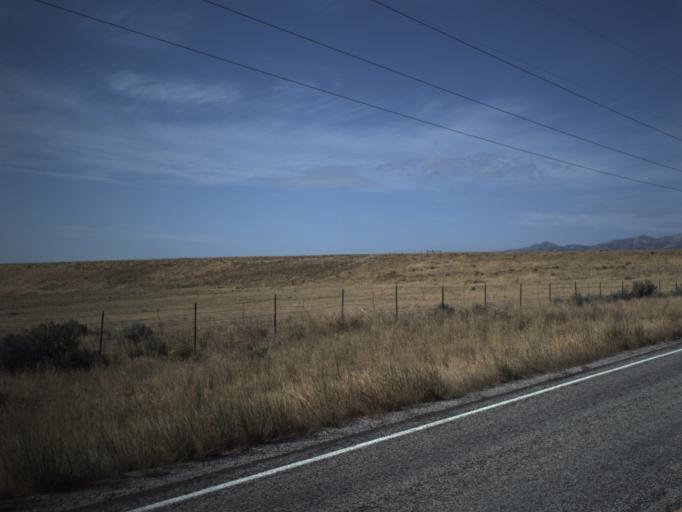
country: US
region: Idaho
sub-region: Oneida County
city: Malad City
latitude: 41.9653
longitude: -113.0541
